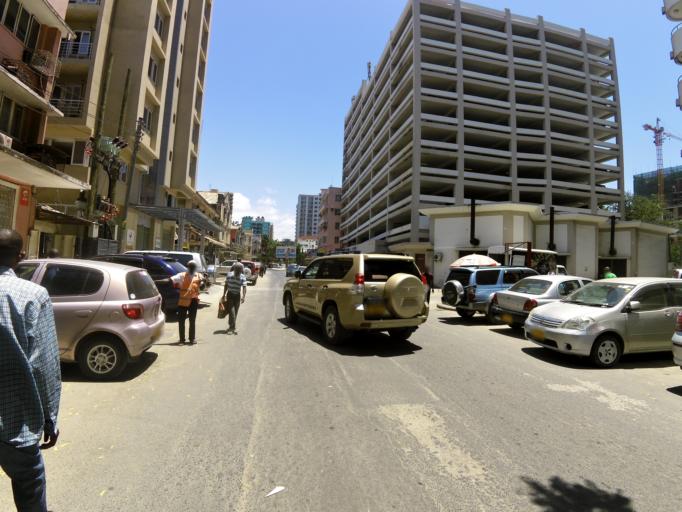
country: TZ
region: Dar es Salaam
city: Dar es Salaam
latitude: -6.8157
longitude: 39.2878
